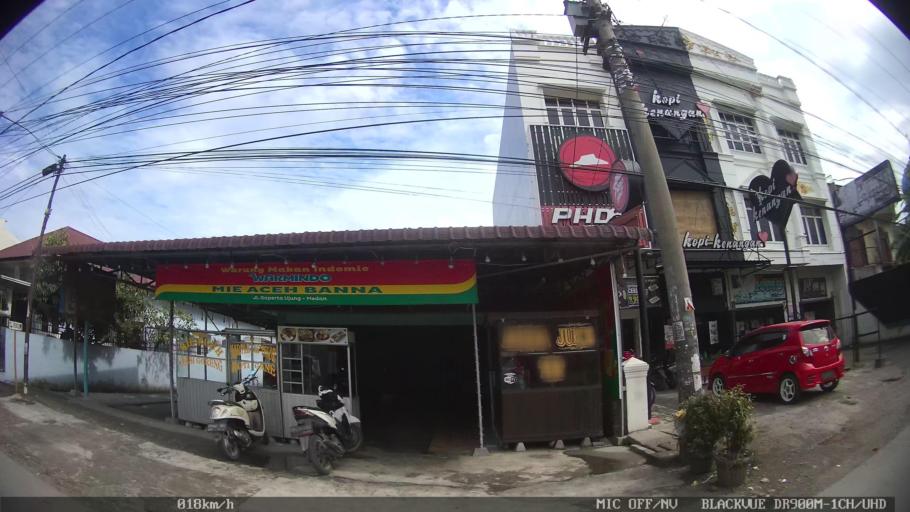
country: ID
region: North Sumatra
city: Sunggal
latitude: 3.6090
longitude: 98.6119
